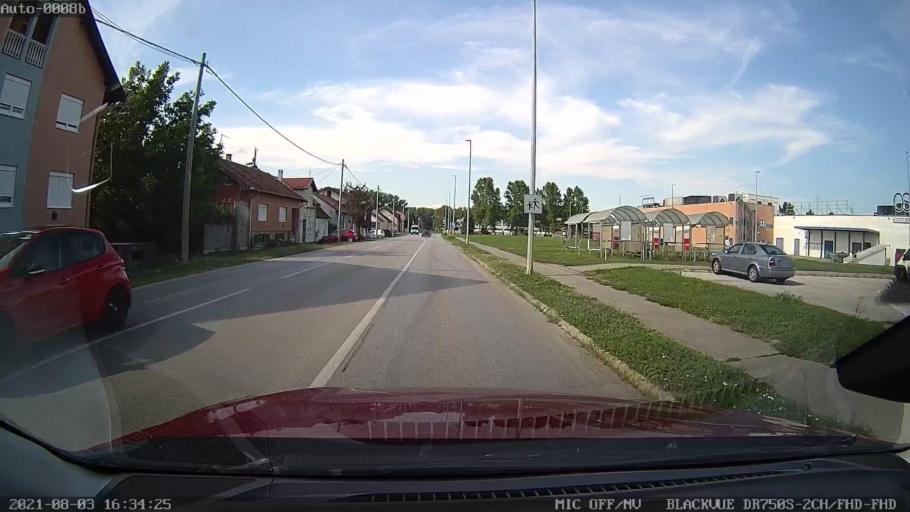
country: HR
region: Osjecko-Baranjska
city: Visnjevac
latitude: 45.5618
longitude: 18.6358
